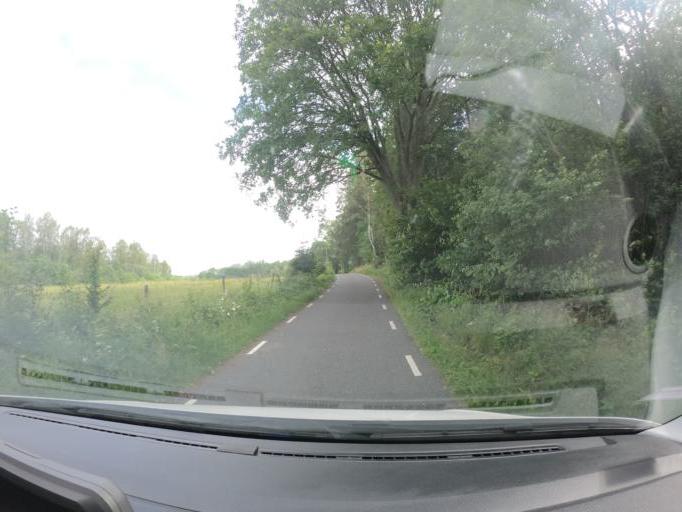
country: SE
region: Skane
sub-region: Eslovs Kommun
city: Stehag
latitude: 56.0131
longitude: 13.3957
